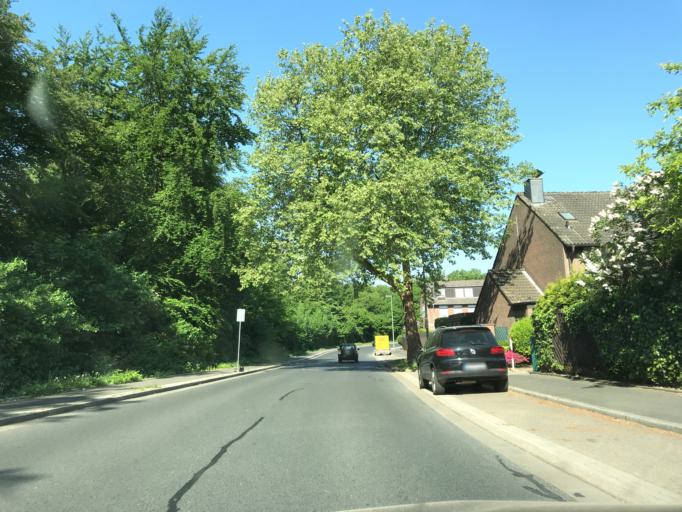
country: DE
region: North Rhine-Westphalia
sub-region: Regierungsbezirk Dusseldorf
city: Essen
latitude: 51.4731
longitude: 7.0617
